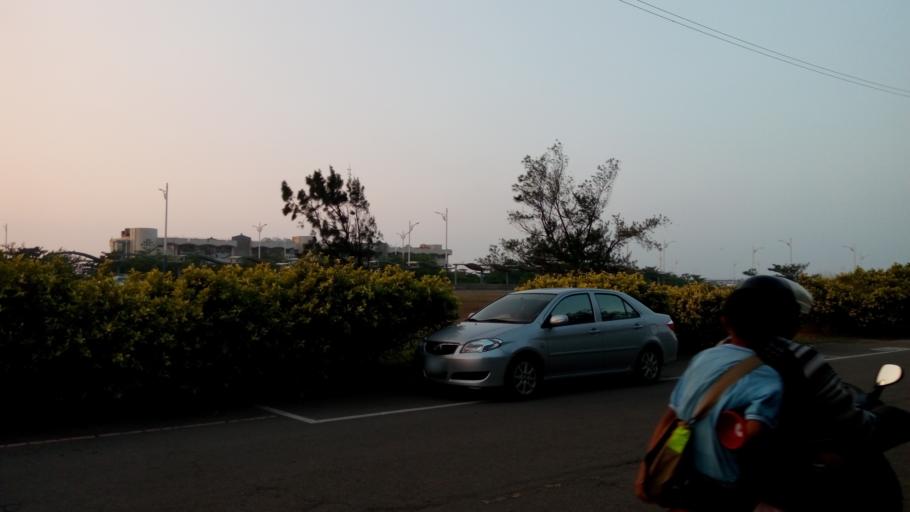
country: TW
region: Taiwan
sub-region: Hsinchu
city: Hsinchu
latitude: 24.8467
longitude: 120.9266
